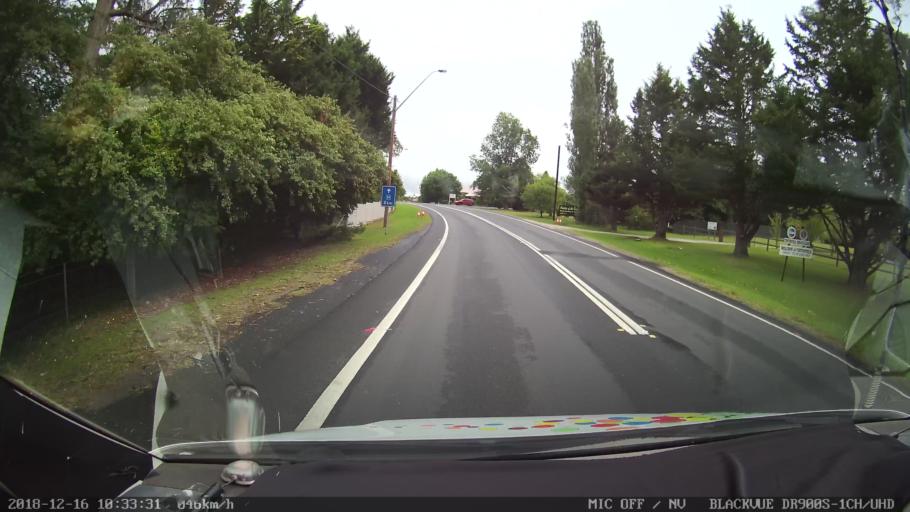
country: AU
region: New South Wales
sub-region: Tenterfield Municipality
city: Carrolls Creek
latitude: -29.0645
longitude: 152.0166
